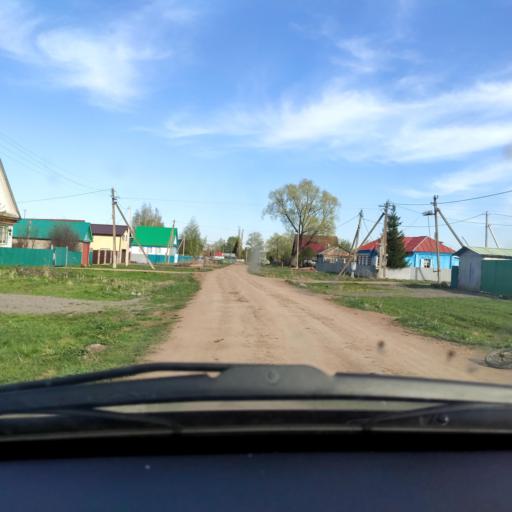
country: RU
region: Bashkortostan
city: Asanovo
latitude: 55.0012
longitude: 55.4895
